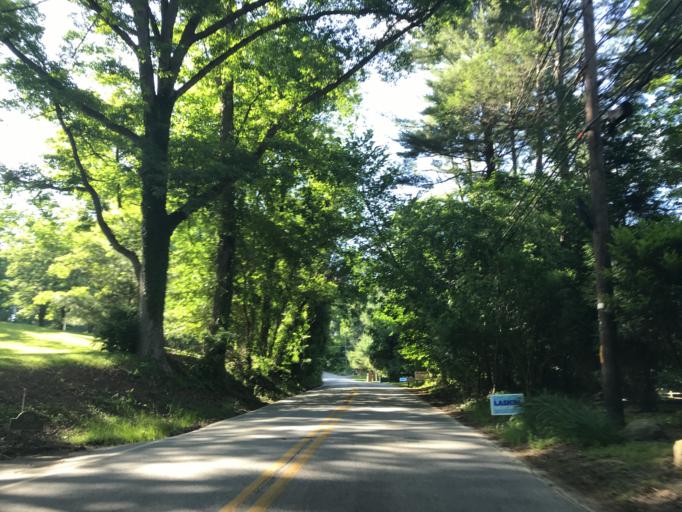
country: US
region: Maryland
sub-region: Baltimore County
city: Garrison
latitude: 39.4188
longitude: -76.7593
